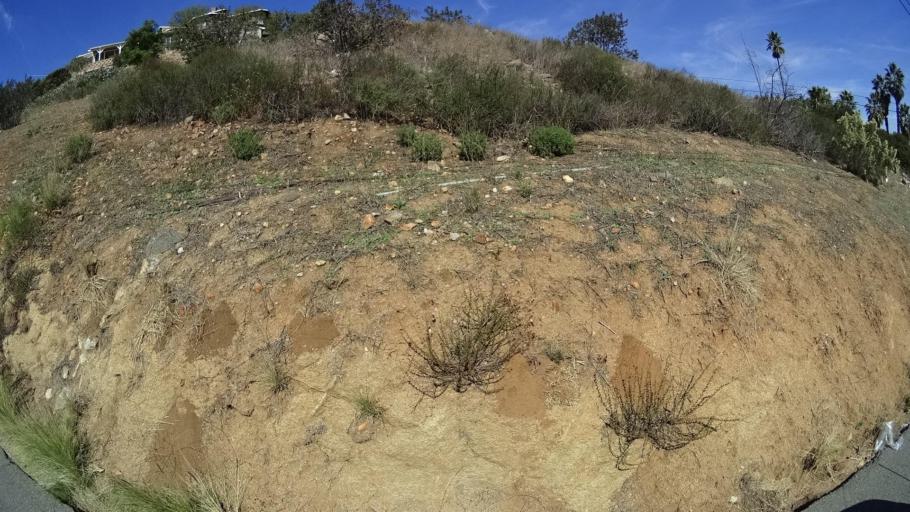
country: US
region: California
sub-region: San Diego County
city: Casa de Oro-Mount Helix
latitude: 32.7568
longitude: -116.9714
